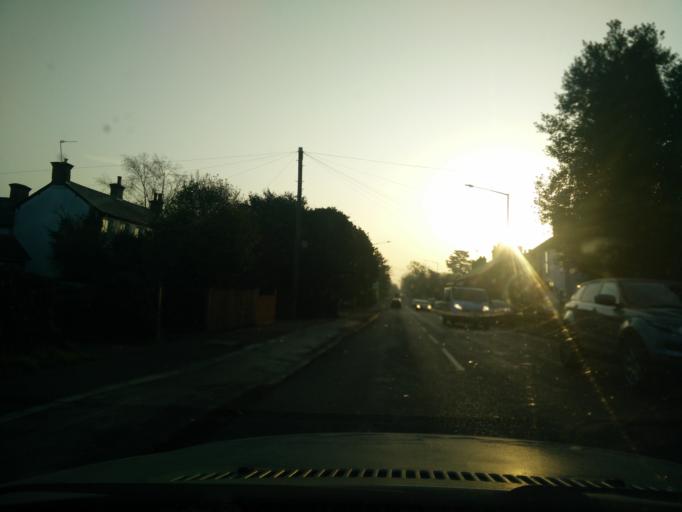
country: GB
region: England
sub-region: Buckinghamshire
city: Little Chalfont
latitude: 51.6717
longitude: -0.5854
